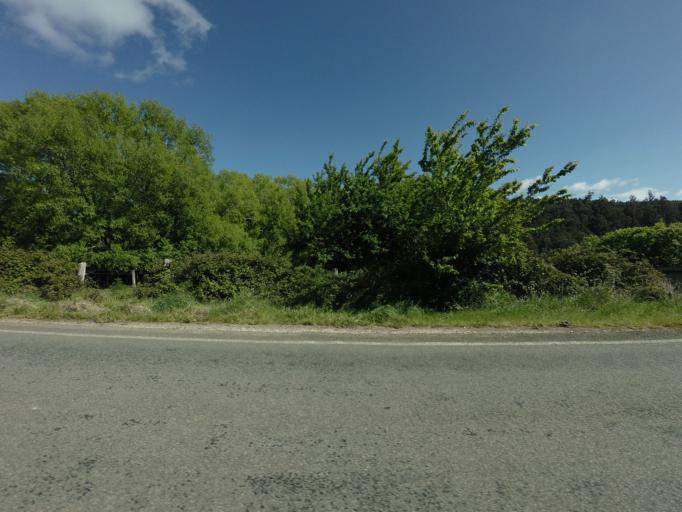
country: AU
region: Tasmania
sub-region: Derwent Valley
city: New Norfolk
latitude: -42.7241
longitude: 146.6767
